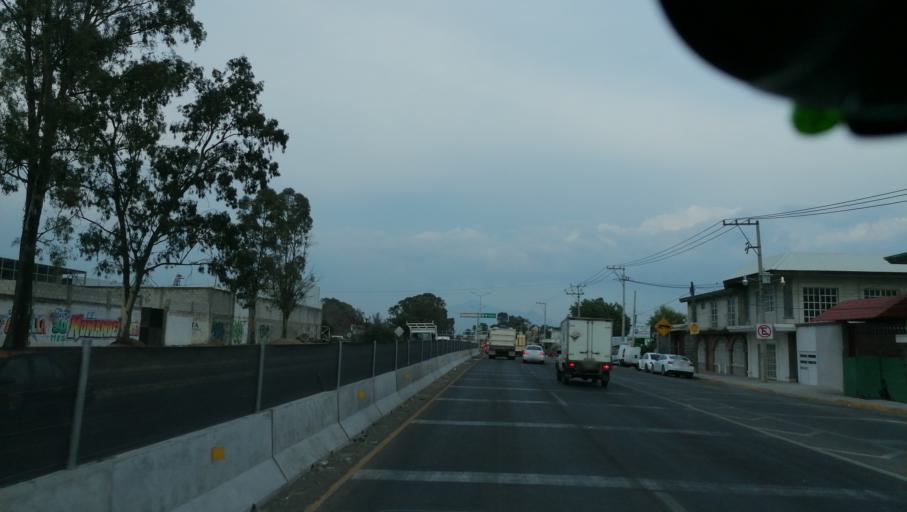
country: MX
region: Puebla
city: Tlazcalancingo
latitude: 19.0208
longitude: -98.3077
